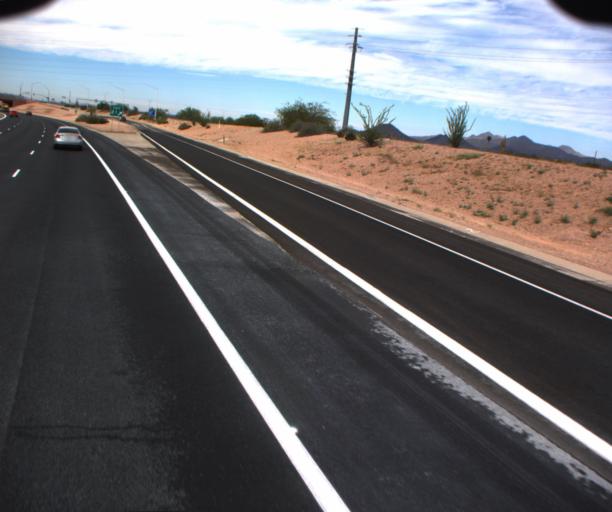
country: US
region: Arizona
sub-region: Maricopa County
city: Mesa
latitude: 33.4802
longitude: -111.7137
